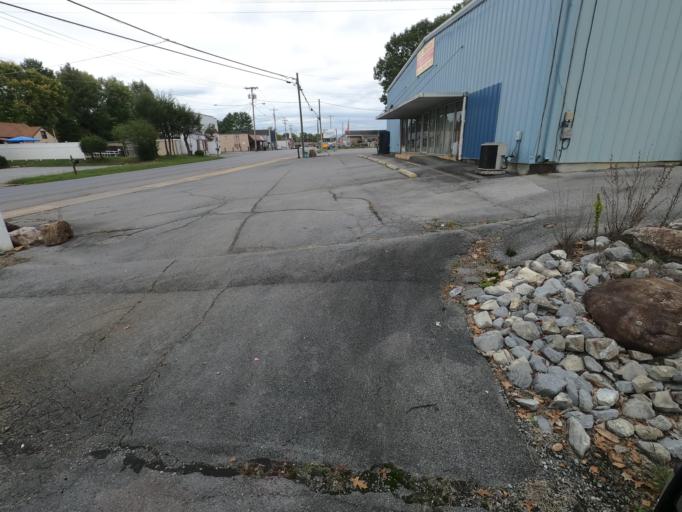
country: US
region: Tennessee
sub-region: Carter County
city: Elizabethton
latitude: 36.3402
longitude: -82.2484
